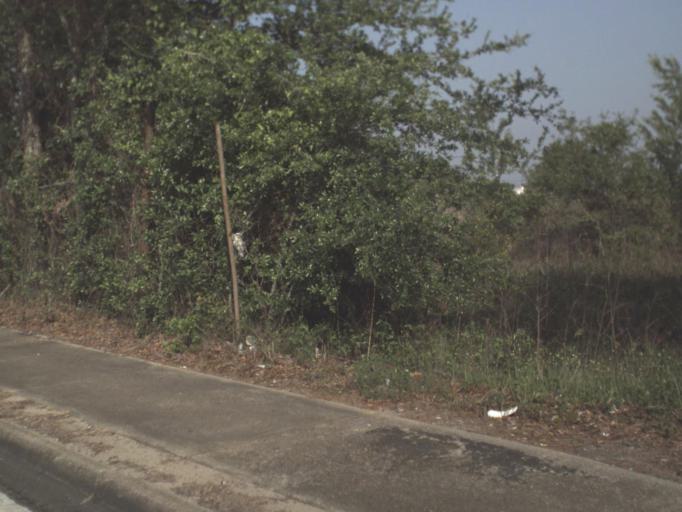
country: US
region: Florida
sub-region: Escambia County
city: Goulding
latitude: 30.4463
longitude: -87.2302
